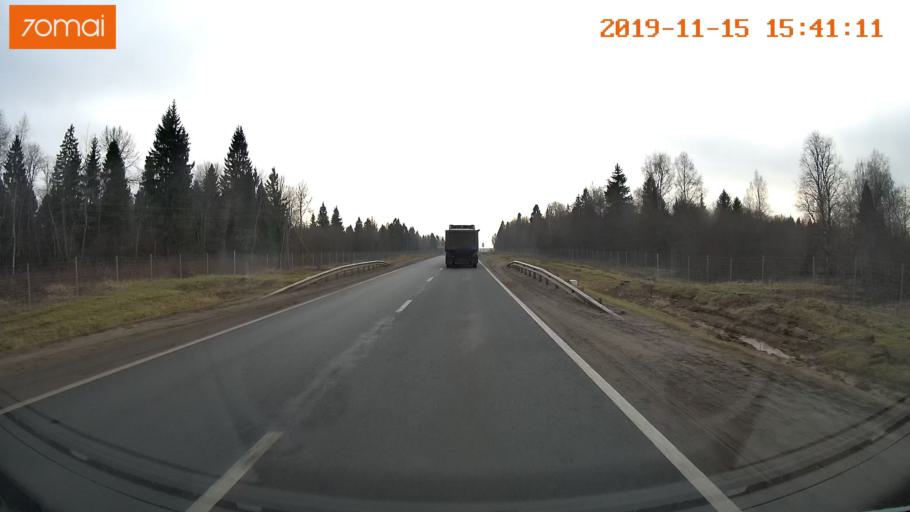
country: RU
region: Jaroslavl
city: Danilov
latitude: 58.0035
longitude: 40.0502
